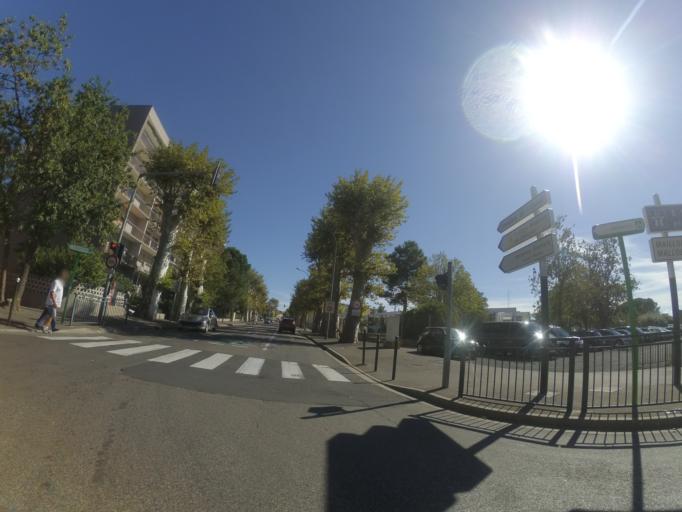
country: FR
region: Languedoc-Roussillon
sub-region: Departement des Pyrenees-Orientales
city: Perpignan
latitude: 42.6896
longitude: 2.8845
